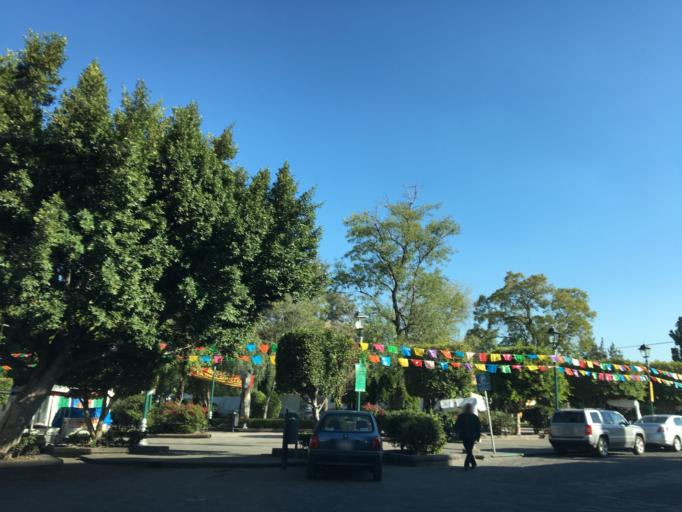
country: MX
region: San Luis Potosi
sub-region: San Luis Potosi
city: San Luis Potosi
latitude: 22.1509
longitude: -100.9932
